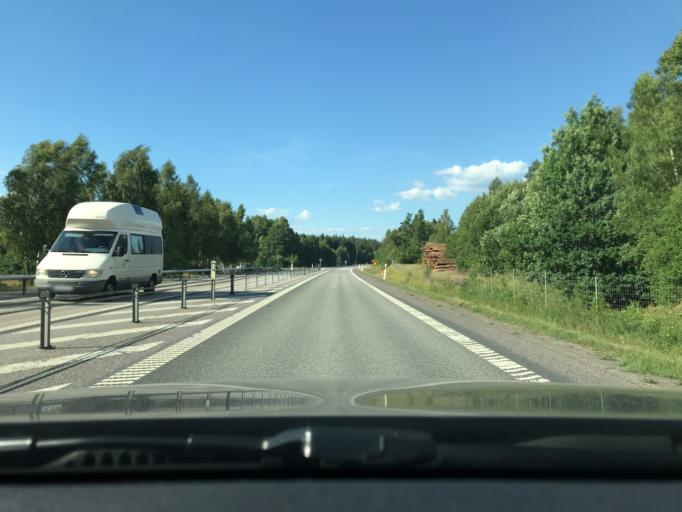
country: SE
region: Skane
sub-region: Osby Kommun
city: Osby
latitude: 56.4019
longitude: 14.0391
